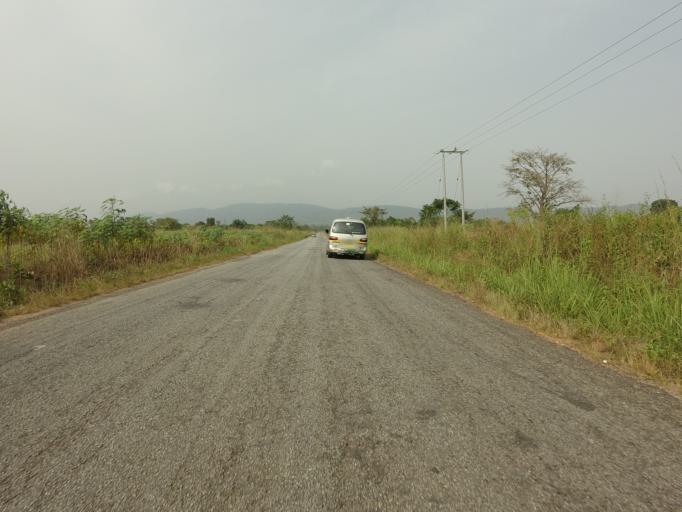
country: GH
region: Volta
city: Ho
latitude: 6.5736
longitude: 0.3511
